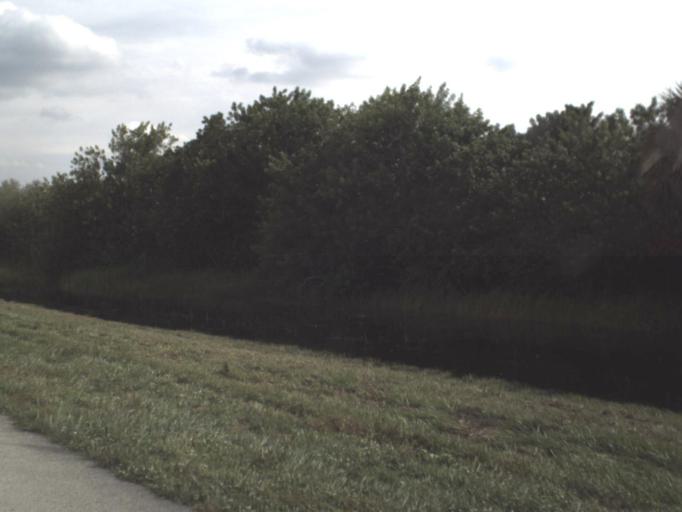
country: US
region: Florida
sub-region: Okeechobee County
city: Taylor Creek
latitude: 27.1880
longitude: -80.7211
